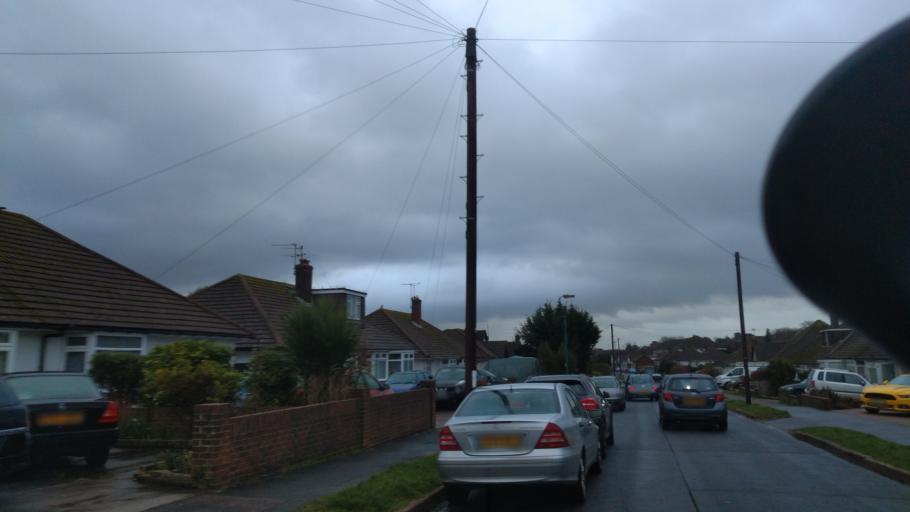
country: GB
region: England
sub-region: East Sussex
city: Eastbourne
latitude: 50.8058
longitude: 0.2447
